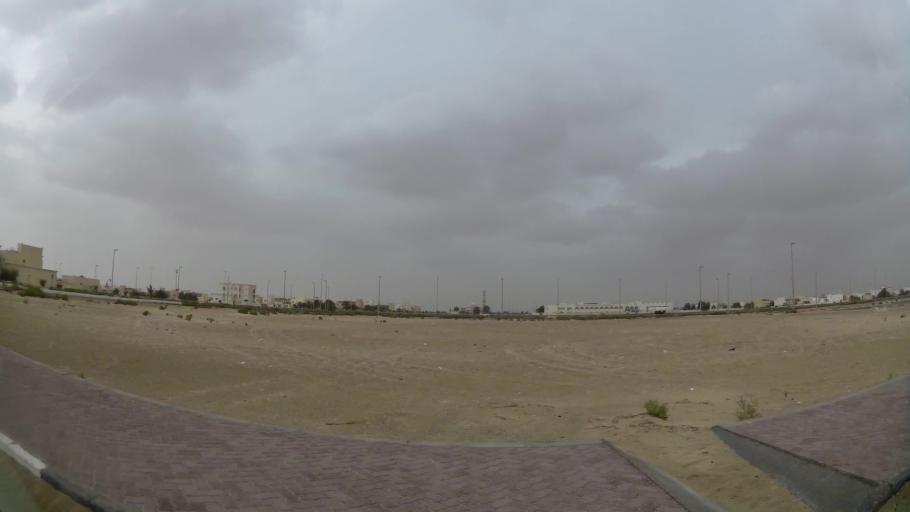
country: AE
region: Abu Dhabi
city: Abu Dhabi
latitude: 24.3719
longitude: 54.6659
